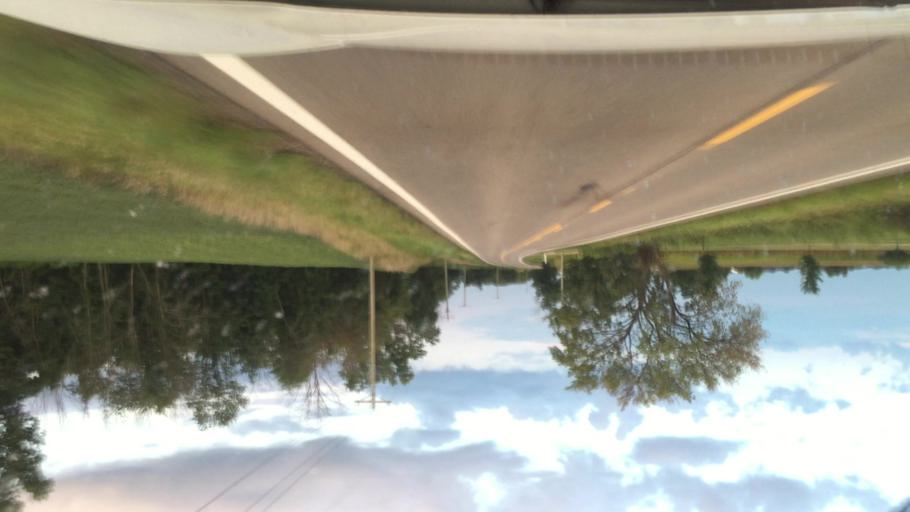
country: US
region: Ohio
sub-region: Champaign County
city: Mechanicsburg
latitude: 40.0504
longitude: -83.5237
